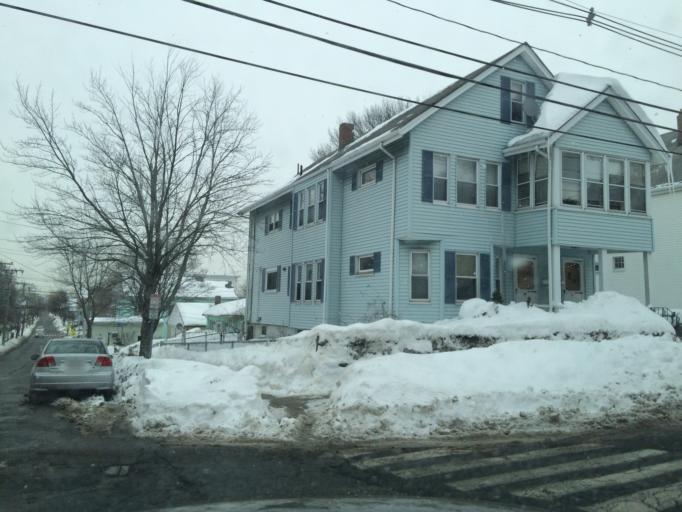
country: US
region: Massachusetts
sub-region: Middlesex County
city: Somerville
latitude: 42.3927
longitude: -71.1120
